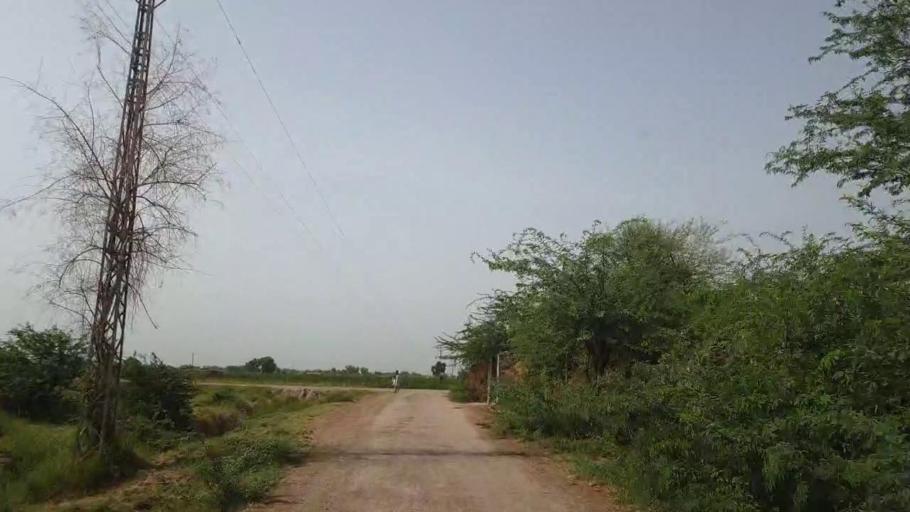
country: PK
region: Sindh
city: Nawabshah
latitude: 26.1099
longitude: 68.4438
